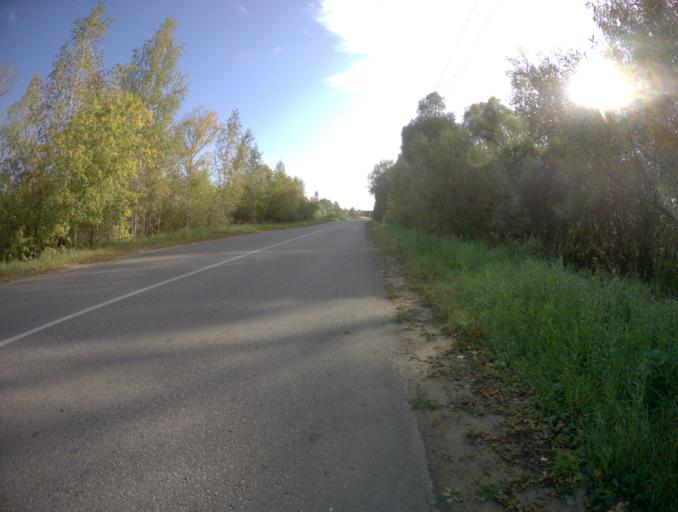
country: RU
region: Moskovskaya
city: Roshal'
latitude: 55.6584
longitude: 39.8385
